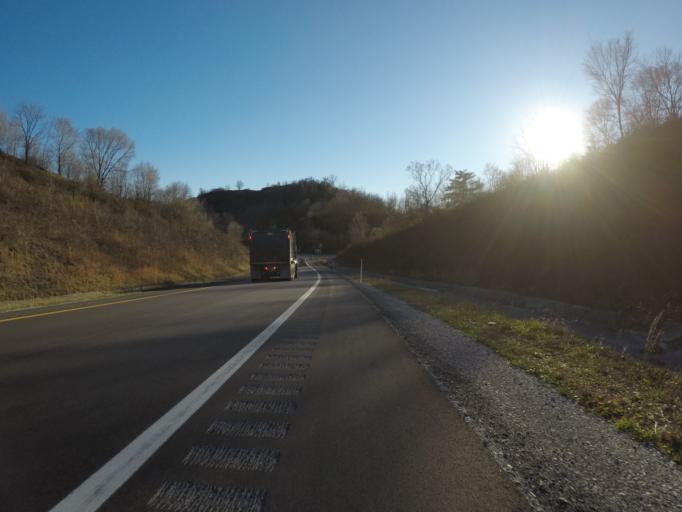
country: US
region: West Virginia
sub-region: Wayne County
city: Kenova
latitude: 38.3711
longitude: -82.5898
